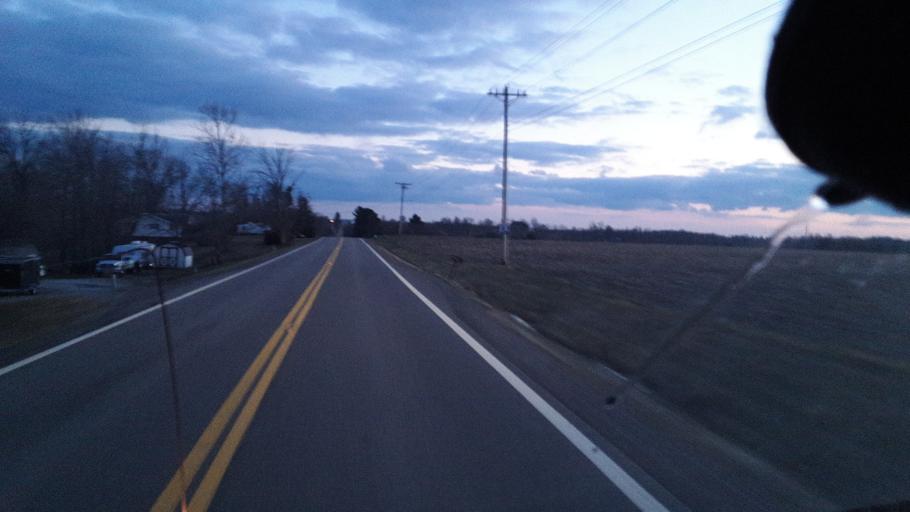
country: US
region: Ohio
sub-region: Perry County
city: Somerset
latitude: 39.7566
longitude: -82.3045
